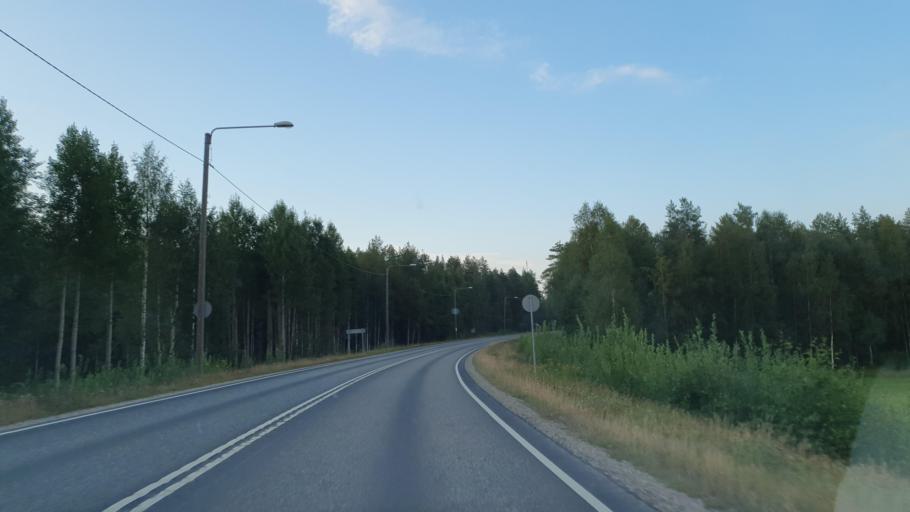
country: FI
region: Kainuu
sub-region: Kehys-Kainuu
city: Hyrynsalmi
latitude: 64.6814
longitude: 28.5109
